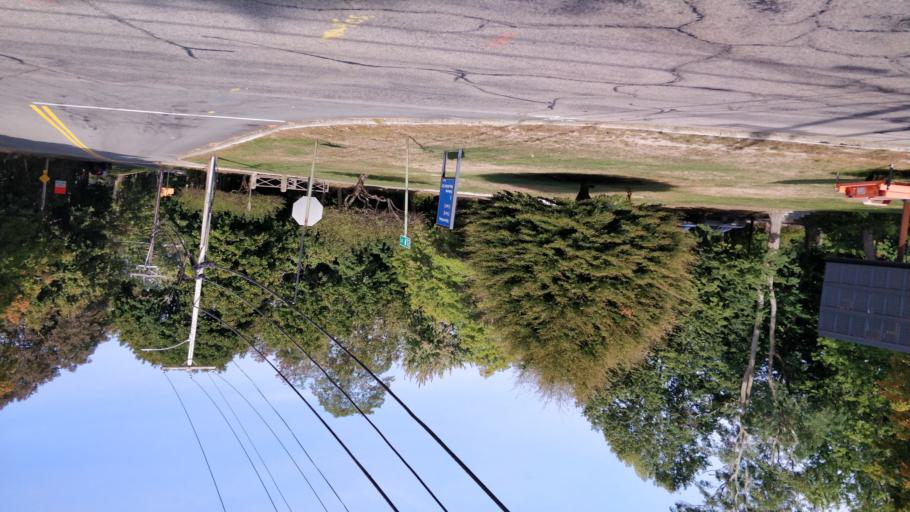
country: US
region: Massachusetts
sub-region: Bristol County
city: Norton Center
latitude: 41.9695
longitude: -71.1821
